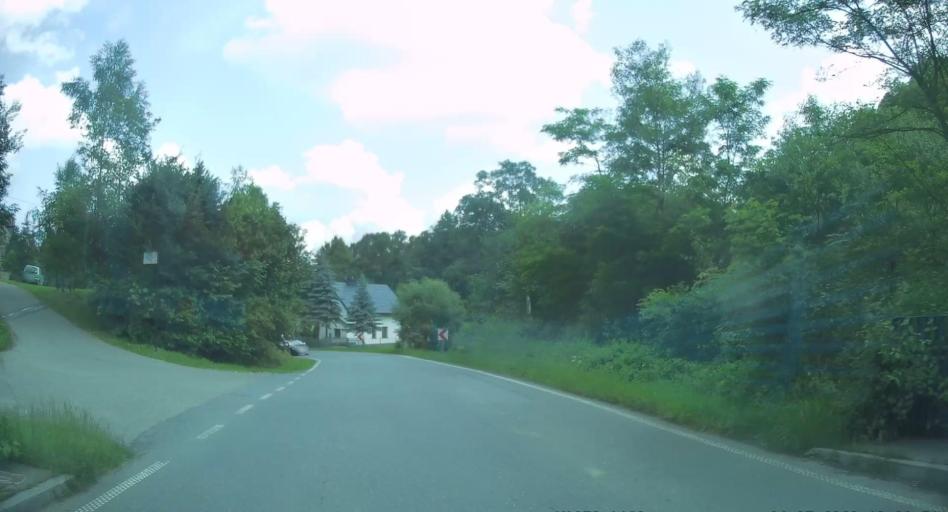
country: PL
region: Lesser Poland Voivodeship
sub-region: Powiat nowosadecki
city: Korzenna
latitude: 49.7237
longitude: 20.7745
